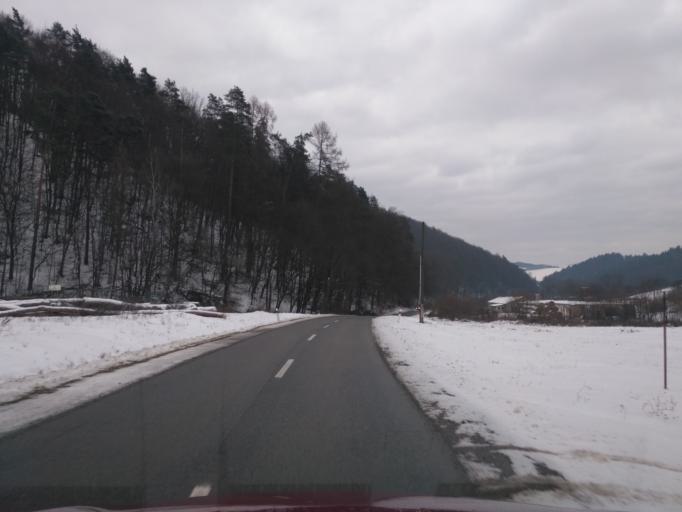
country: SK
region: Presovsky
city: Sabinov
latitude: 48.9652
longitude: 21.0936
